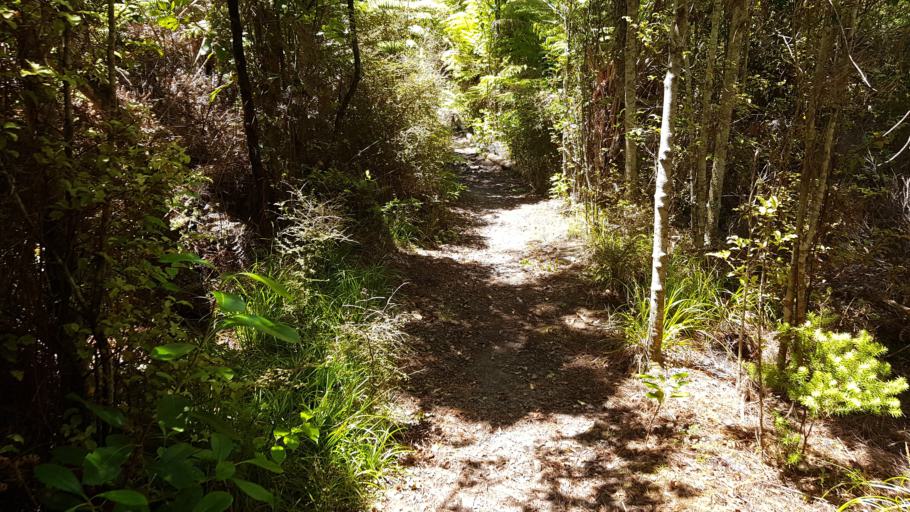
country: NZ
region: Auckland
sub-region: Auckland
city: North Shore
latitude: -36.8227
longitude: 174.7091
